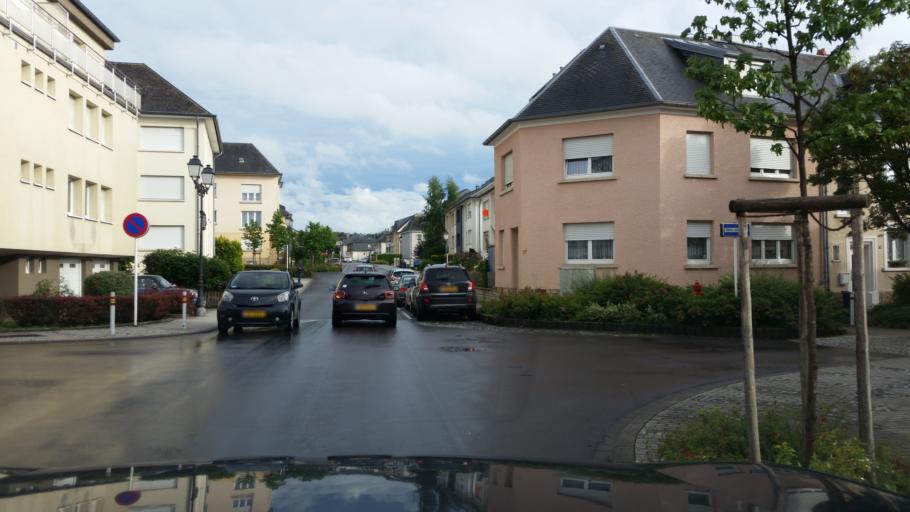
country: LU
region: Luxembourg
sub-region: Canton de Luxembourg
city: Hesperange
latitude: 49.5868
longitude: 6.1380
